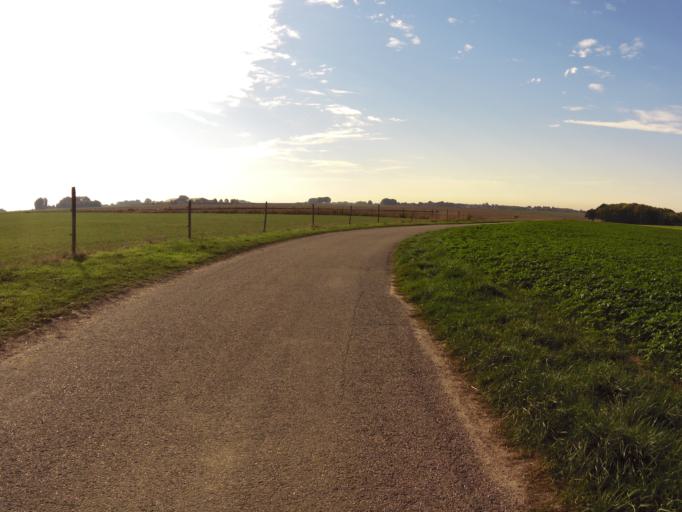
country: NL
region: Limburg
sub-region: Gemeente Schinnen
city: Doenrade
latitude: 50.9675
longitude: 5.8895
